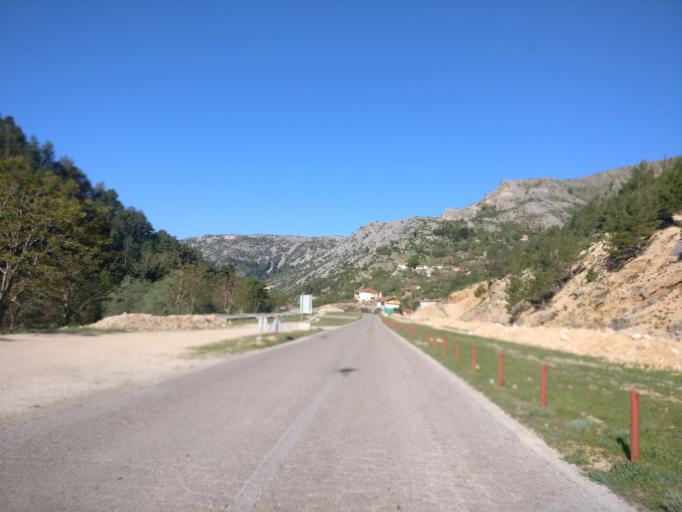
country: BA
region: Federation of Bosnia and Herzegovina
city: Stolac
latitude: 43.0994
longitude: 17.9815
